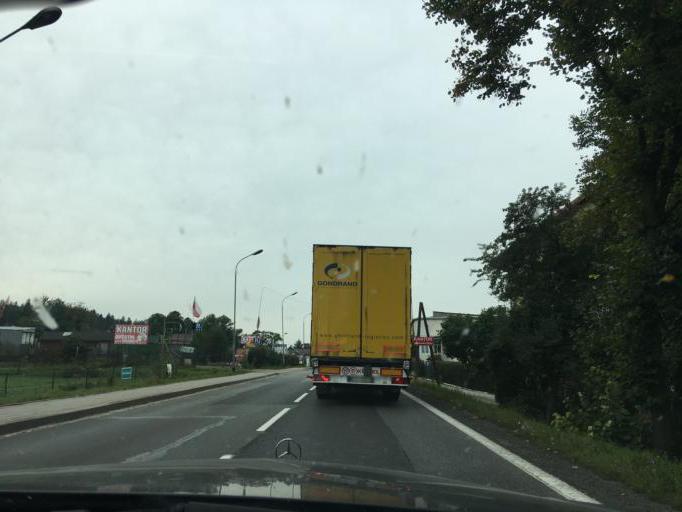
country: PL
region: Lower Silesian Voivodeship
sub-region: Powiat klodzki
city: Kudowa-Zdroj
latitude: 50.4348
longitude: 16.2203
